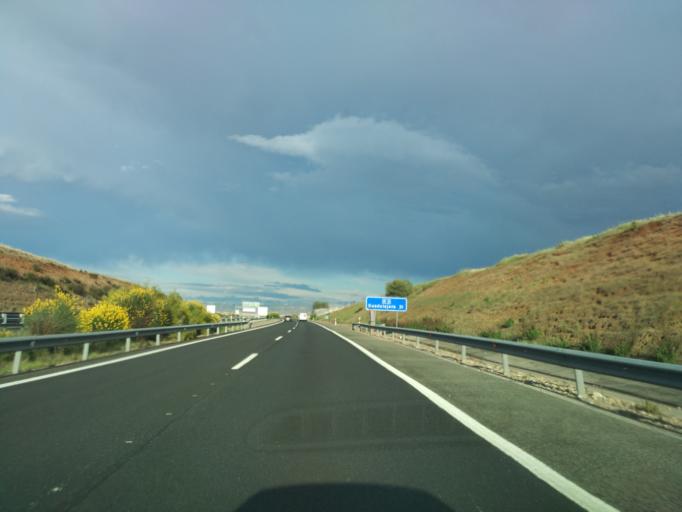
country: ES
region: Madrid
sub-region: Provincia de Madrid
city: Ajalvir
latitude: 40.5066
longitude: -3.4776
